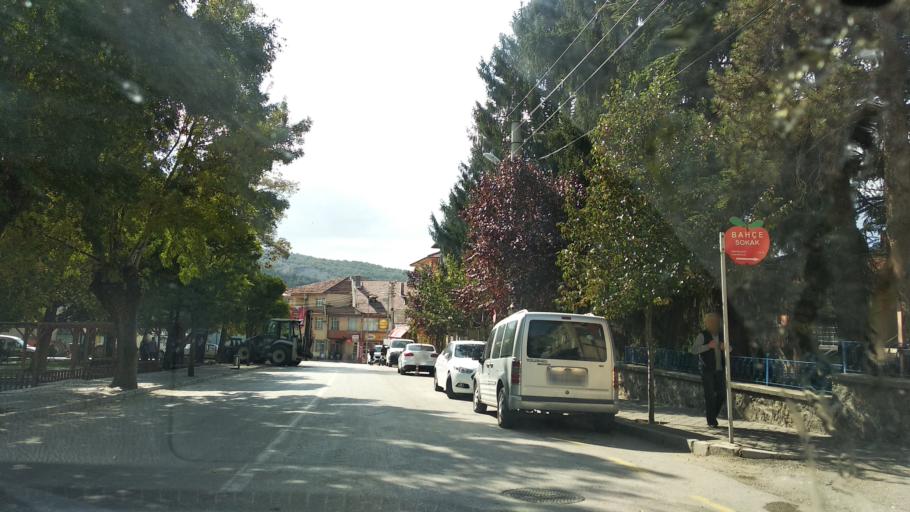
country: TR
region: Bolu
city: Seben
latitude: 40.4090
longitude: 31.5726
